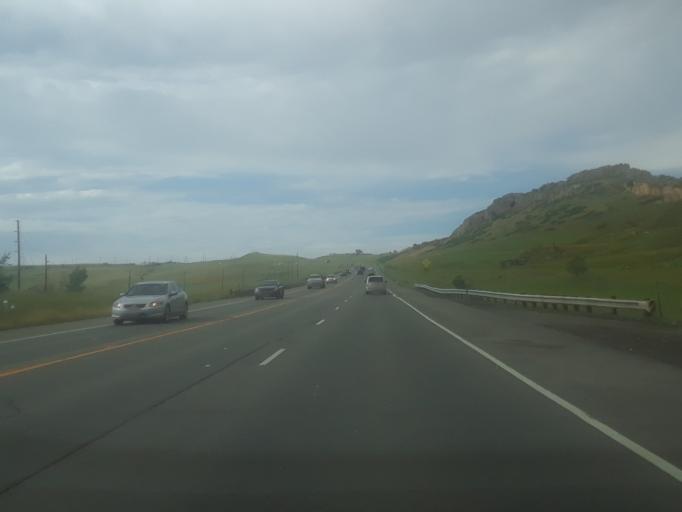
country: US
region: Colorado
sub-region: Jefferson County
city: Golden
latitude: 39.8484
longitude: -105.2339
